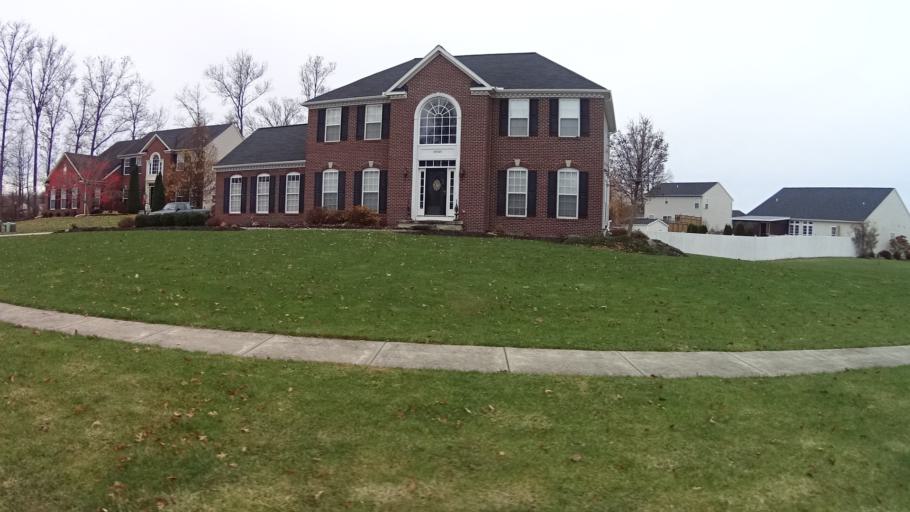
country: US
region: Ohio
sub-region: Lorain County
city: North Ridgeville
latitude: 41.3599
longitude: -81.9964
